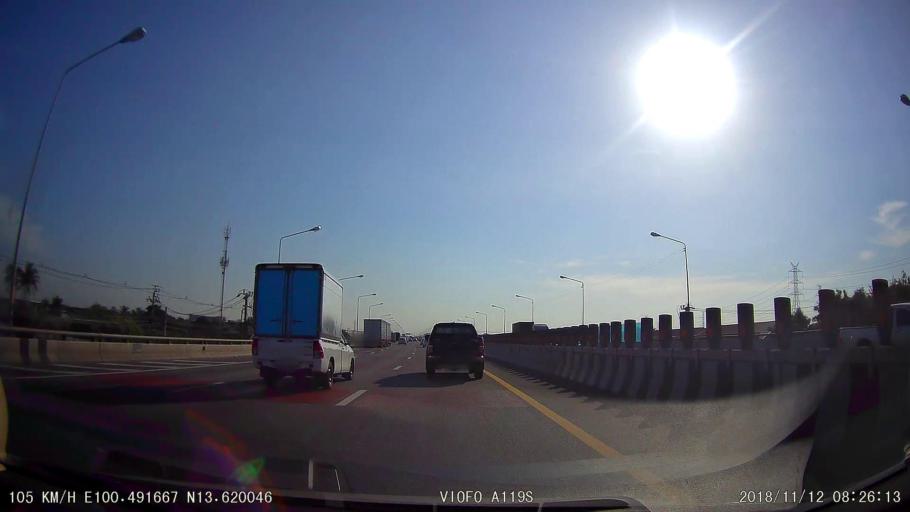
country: TH
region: Bangkok
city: Thung Khru
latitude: 13.6200
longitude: 100.4921
